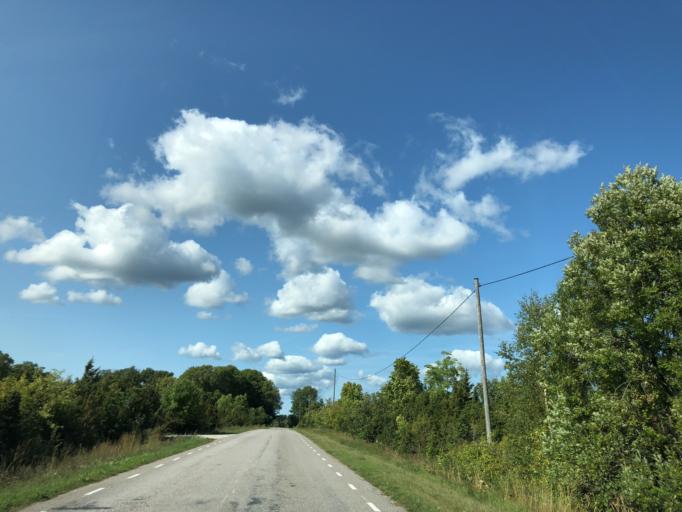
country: EE
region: Hiiumaa
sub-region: Kaerdla linn
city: Kardla
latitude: 58.7948
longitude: 22.7674
